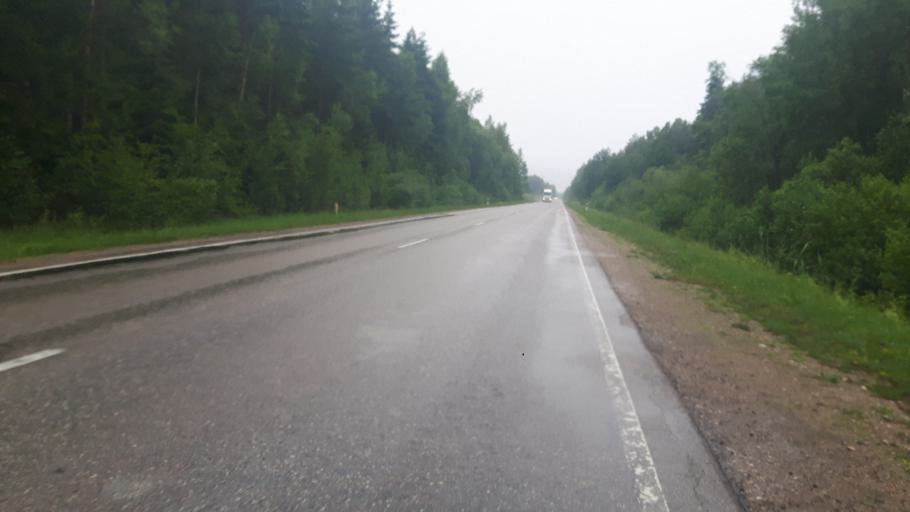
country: LV
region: Rucavas
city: Rucava
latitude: 56.1121
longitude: 21.1408
